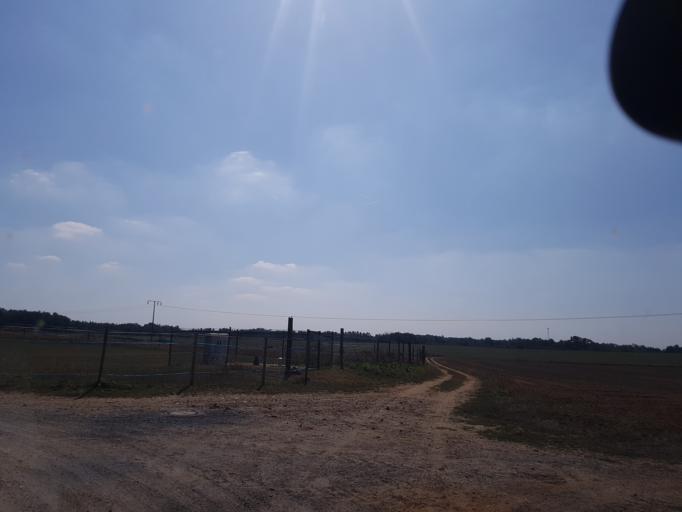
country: DE
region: Brandenburg
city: Hohenleipisch
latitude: 51.4838
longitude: 13.5356
